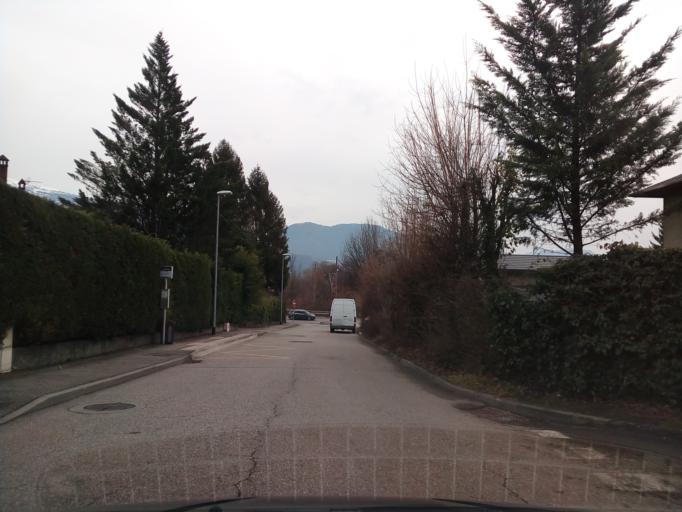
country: FR
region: Rhone-Alpes
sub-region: Departement de l'Isere
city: Corenc
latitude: 45.2153
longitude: 5.7795
